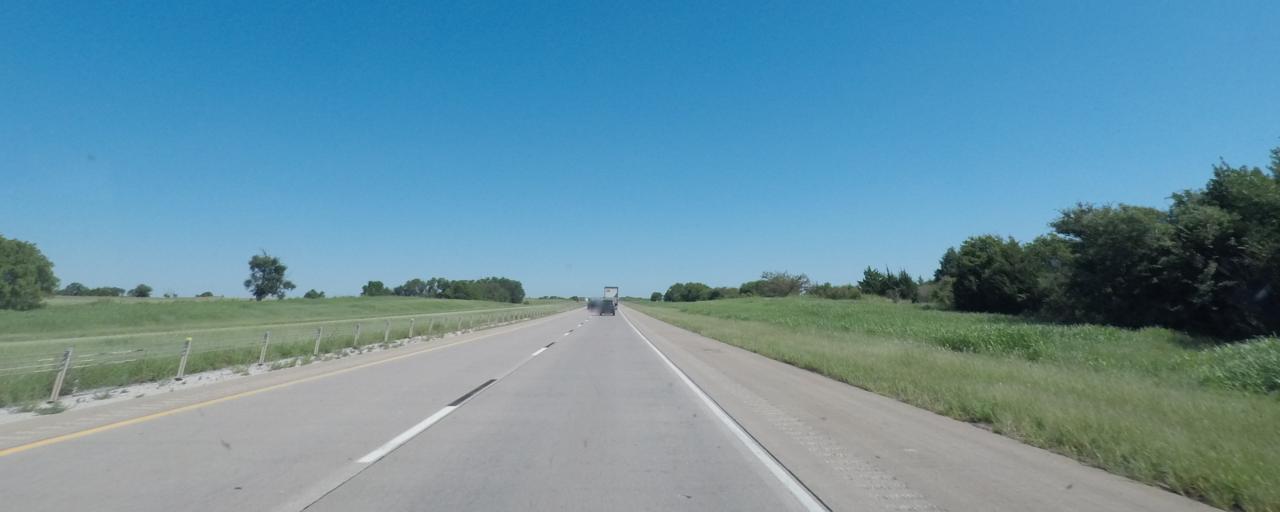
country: US
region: Oklahoma
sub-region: Noble County
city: Perry
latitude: 36.4385
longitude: -97.3269
